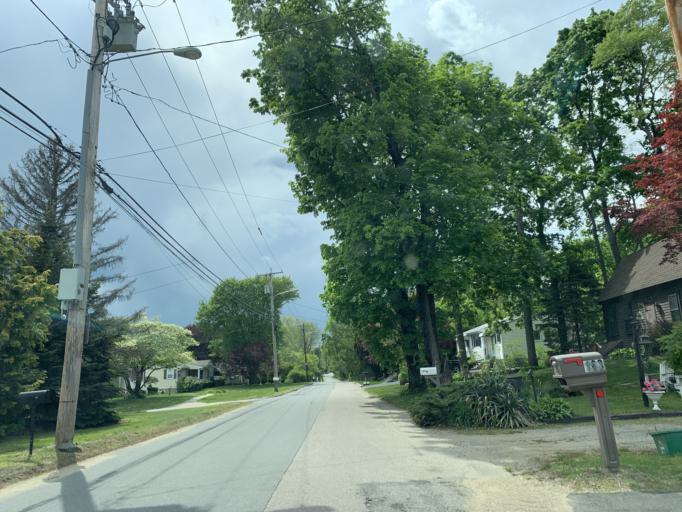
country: US
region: Rhode Island
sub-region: Providence County
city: Johnston
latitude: 41.8053
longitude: -71.4776
